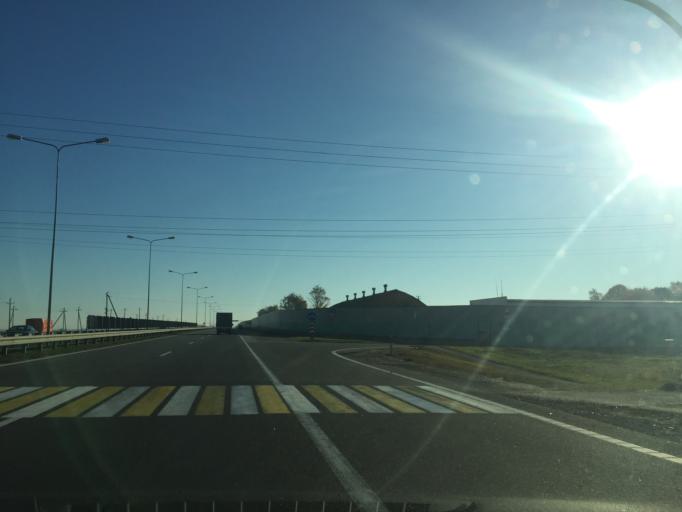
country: BY
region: Minsk
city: Smilavichy
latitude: 53.7595
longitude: 28.0032
